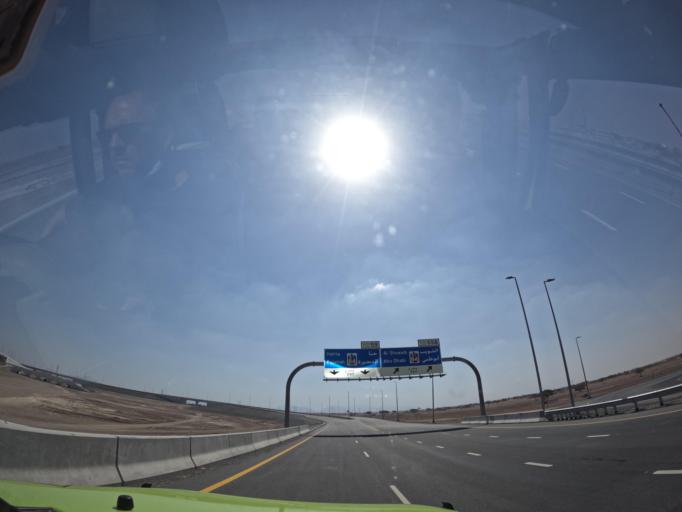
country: AE
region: Ash Shariqah
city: Adh Dhayd
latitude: 24.9101
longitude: 55.7969
